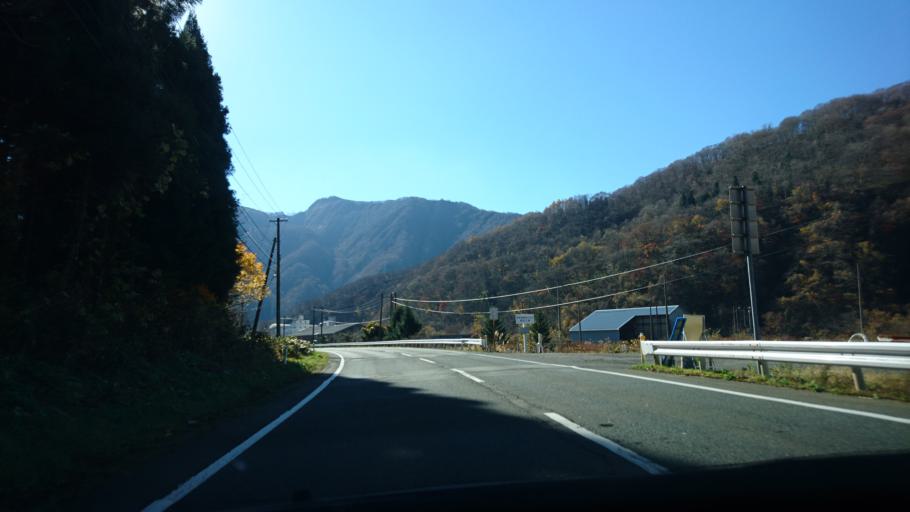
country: JP
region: Iwate
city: Kitakami
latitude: 39.3075
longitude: 140.9021
